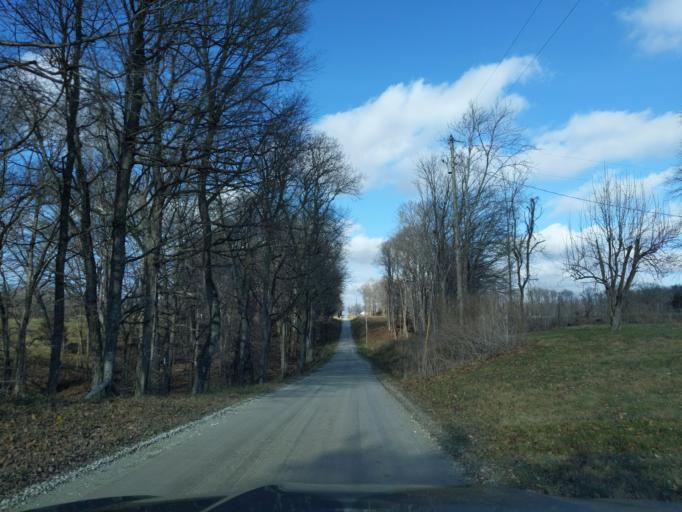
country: US
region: Indiana
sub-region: Decatur County
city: Greensburg
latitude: 39.2570
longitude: -85.4842
